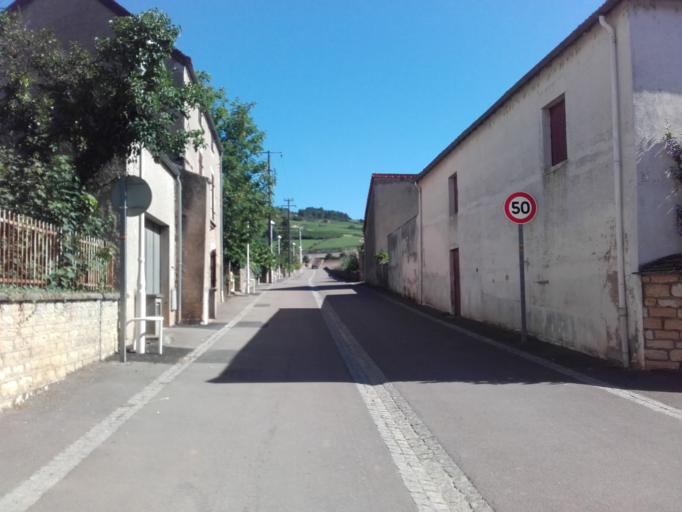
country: FR
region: Bourgogne
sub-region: Departement de Saone-et-Loire
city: Chagny
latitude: 46.9121
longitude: 4.7009
